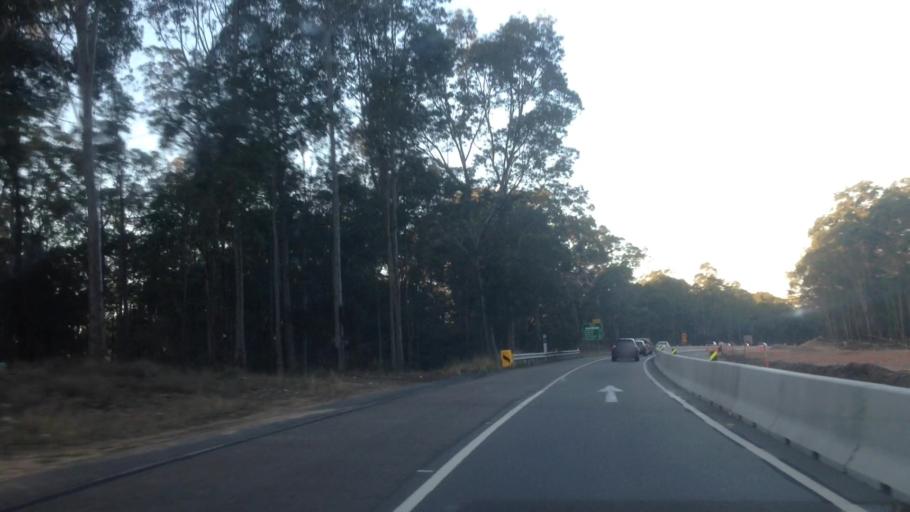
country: AU
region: New South Wales
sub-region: Wyong Shire
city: Jilliby
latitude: -33.2162
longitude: 151.4428
